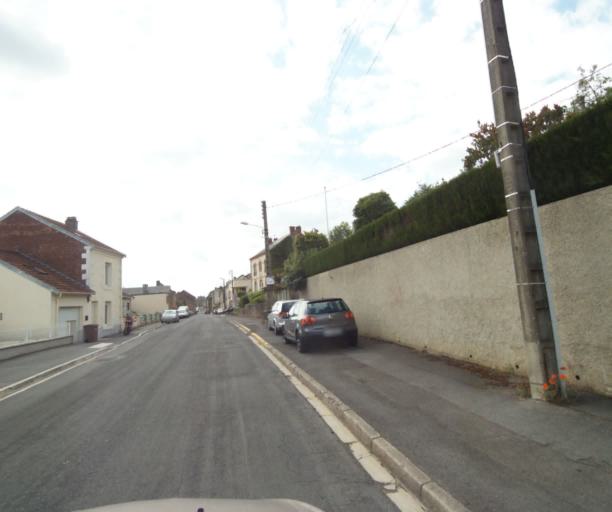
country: FR
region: Champagne-Ardenne
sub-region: Departement des Ardennes
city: Villers-Semeuse
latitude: 49.7581
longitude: 4.7422
